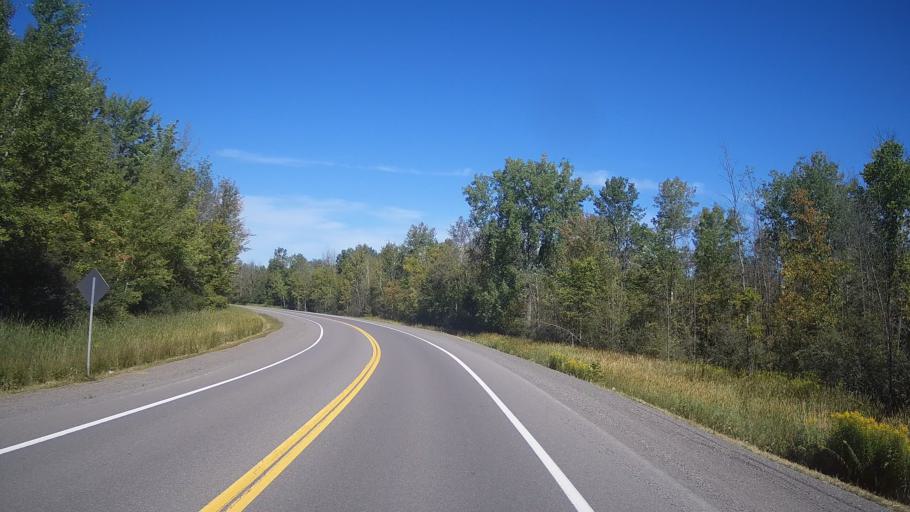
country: CA
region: Ontario
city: Bells Corners
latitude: 45.0769
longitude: -75.6483
